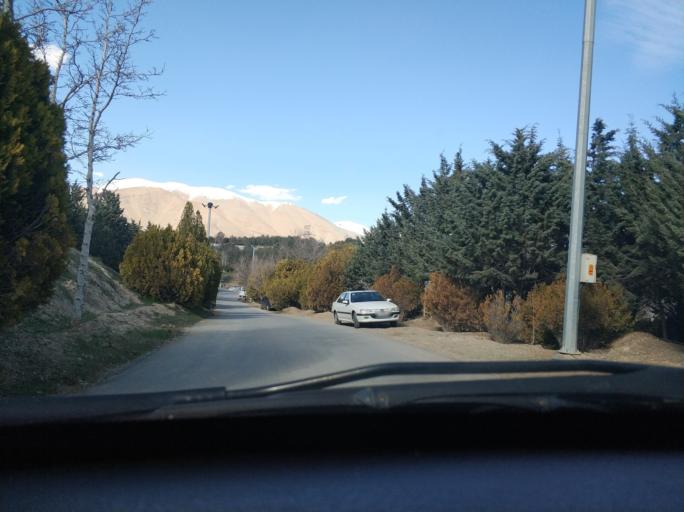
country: IR
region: Tehran
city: Tajrish
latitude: 35.8029
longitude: 51.5680
